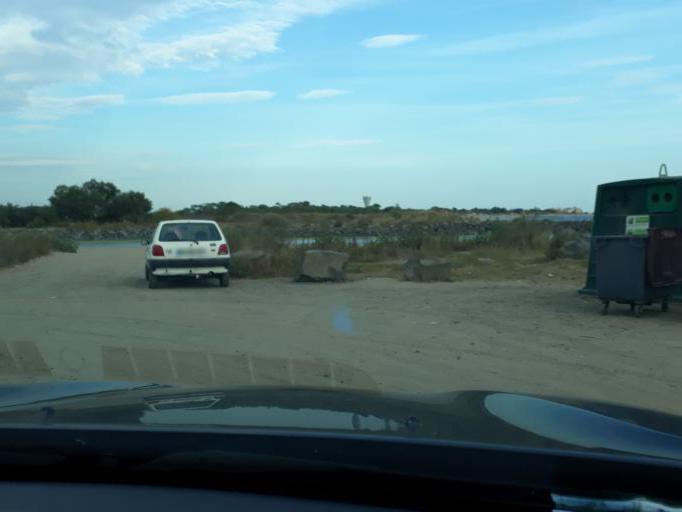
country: FR
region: Languedoc-Roussillon
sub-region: Departement de l'Herault
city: Vias
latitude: 43.2907
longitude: 3.4281
